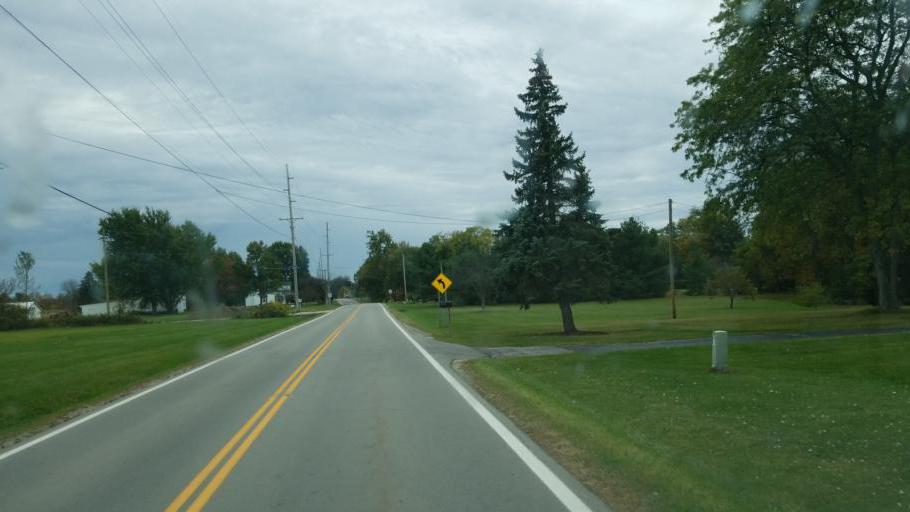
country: US
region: Ohio
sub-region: Huron County
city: Wakeman
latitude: 41.2616
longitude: -82.3968
